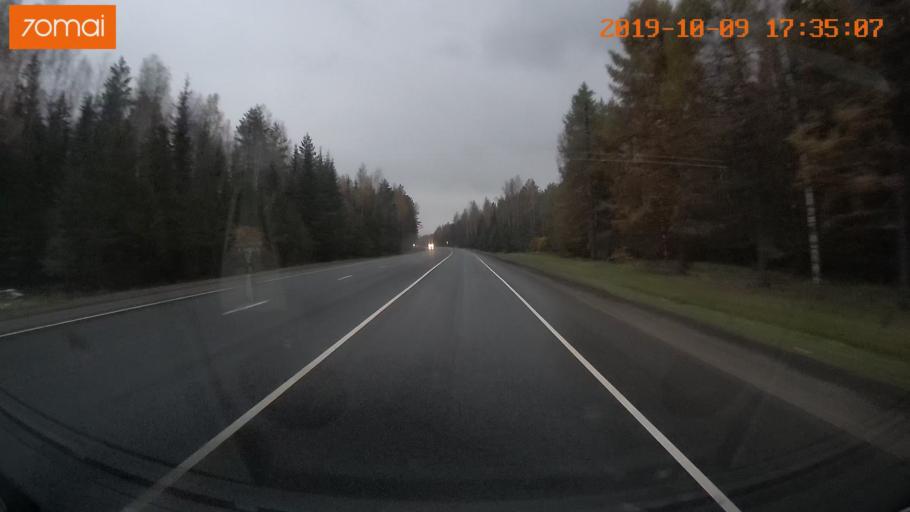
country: RU
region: Ivanovo
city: Bogorodskoye
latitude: 57.0984
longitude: 41.0047
